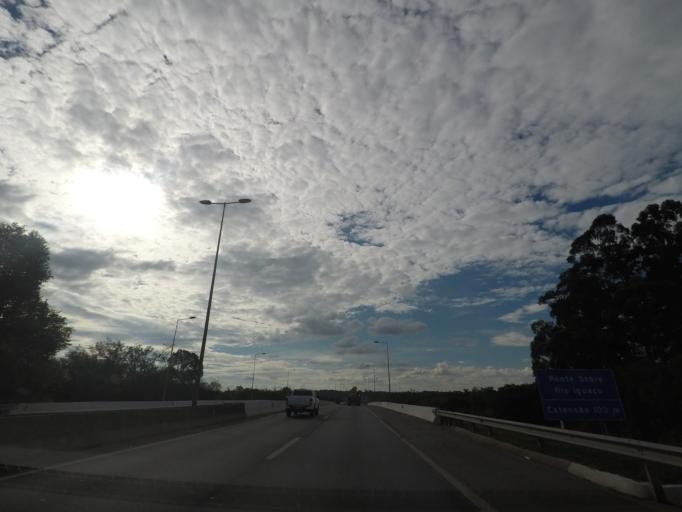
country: BR
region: Parana
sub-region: Araucaria
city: Araucaria
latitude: -25.6234
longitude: -49.3154
